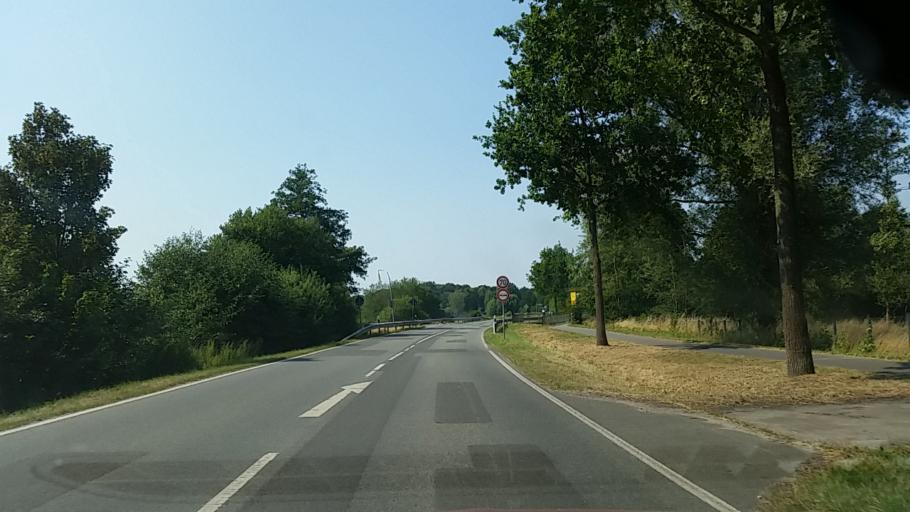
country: DE
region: Schleswig-Holstein
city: Dahmker
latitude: 53.5991
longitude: 10.4482
